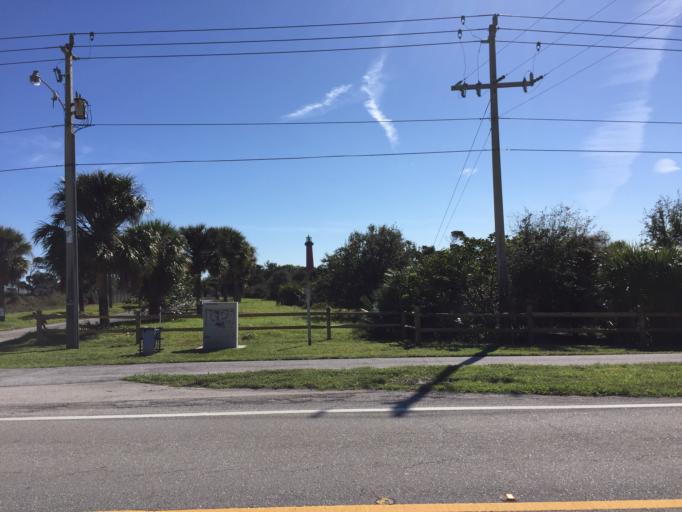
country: US
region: Florida
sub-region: Palm Beach County
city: Jupiter
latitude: 26.9524
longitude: -80.0824
